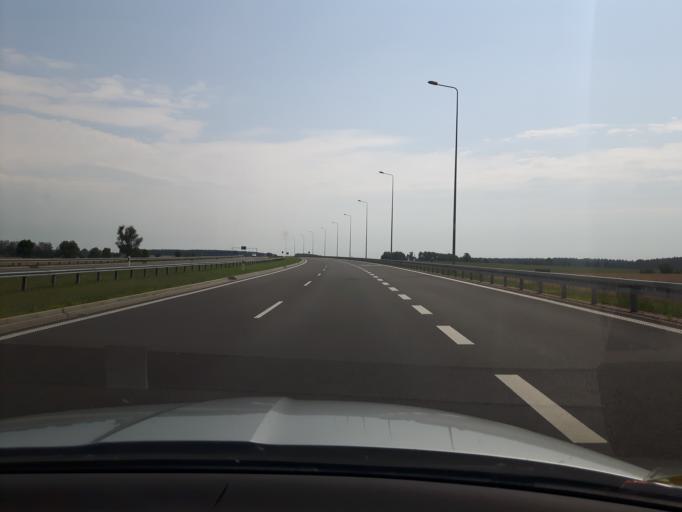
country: PL
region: Masovian Voivodeship
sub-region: Powiat mlawski
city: Wieczfnia Koscielna
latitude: 53.2257
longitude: 20.4197
